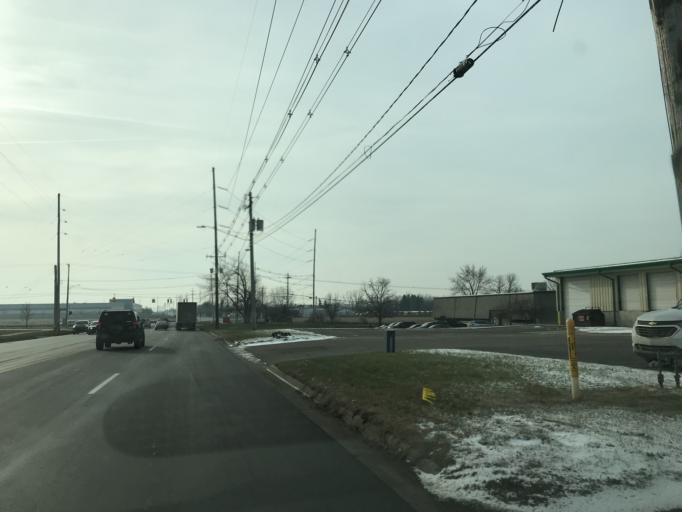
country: US
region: Michigan
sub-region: Ottawa County
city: Holland
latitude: 42.7700
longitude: -86.0774
